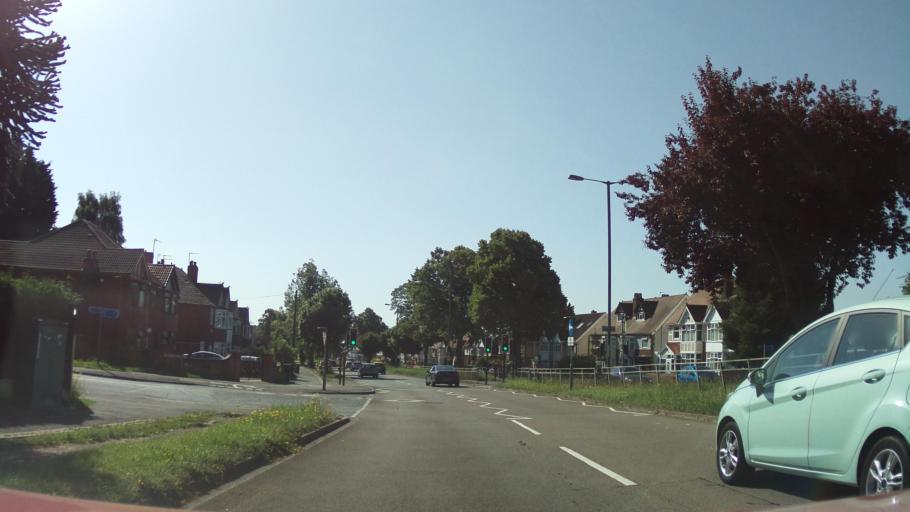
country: GB
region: England
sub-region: Derby
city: Derby
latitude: 52.9054
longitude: -1.4986
